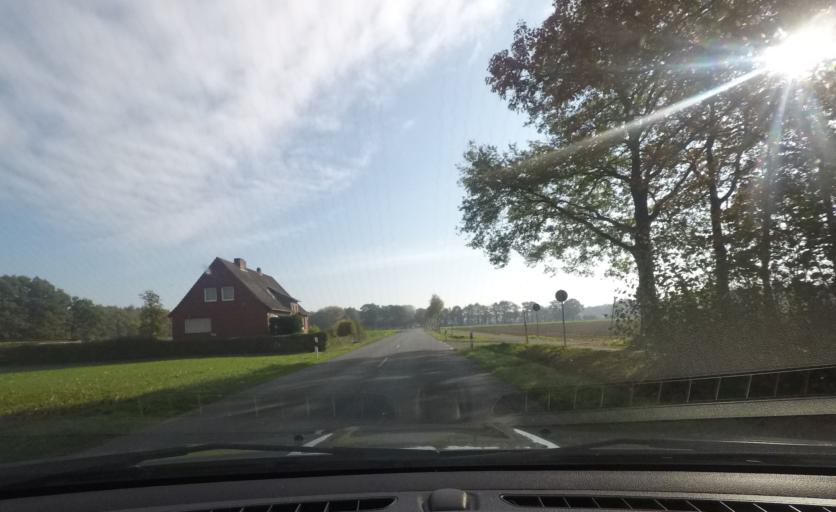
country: DE
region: North Rhine-Westphalia
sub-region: Regierungsbezirk Munster
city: Dulmen
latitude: 51.8479
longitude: 7.2234
